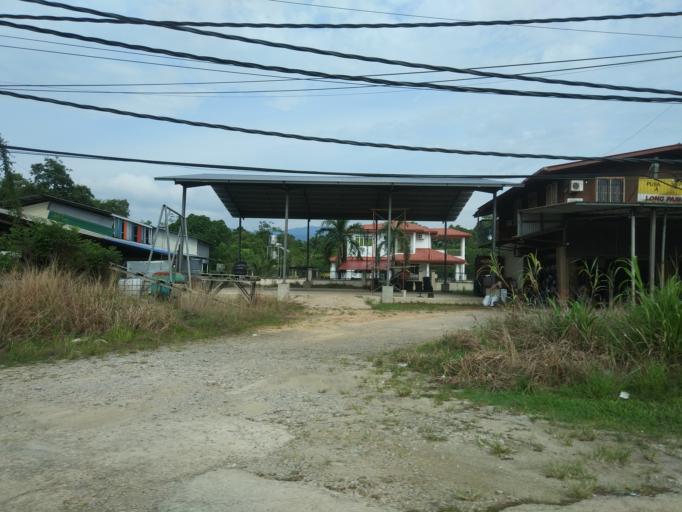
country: MY
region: Sabah
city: Beaufort
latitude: 5.0674
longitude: 115.5503
